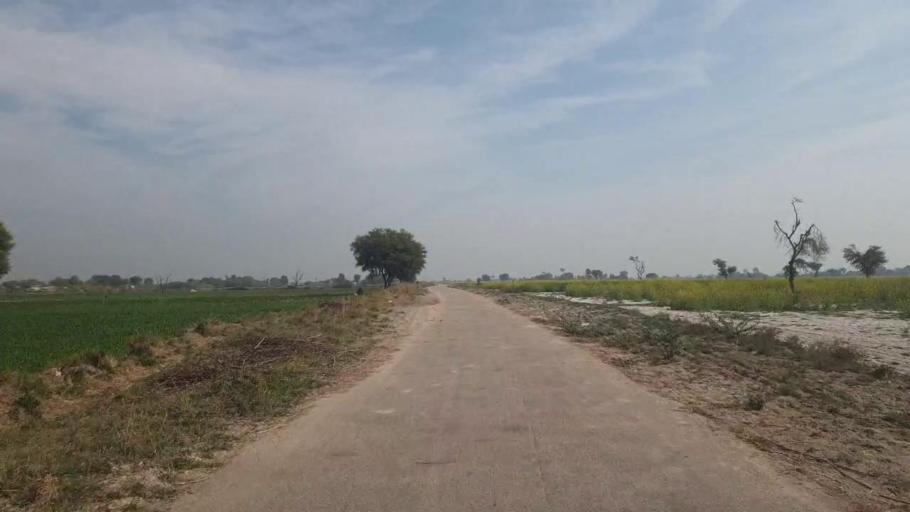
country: PK
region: Sindh
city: Nawabshah
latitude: 26.1240
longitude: 68.4929
